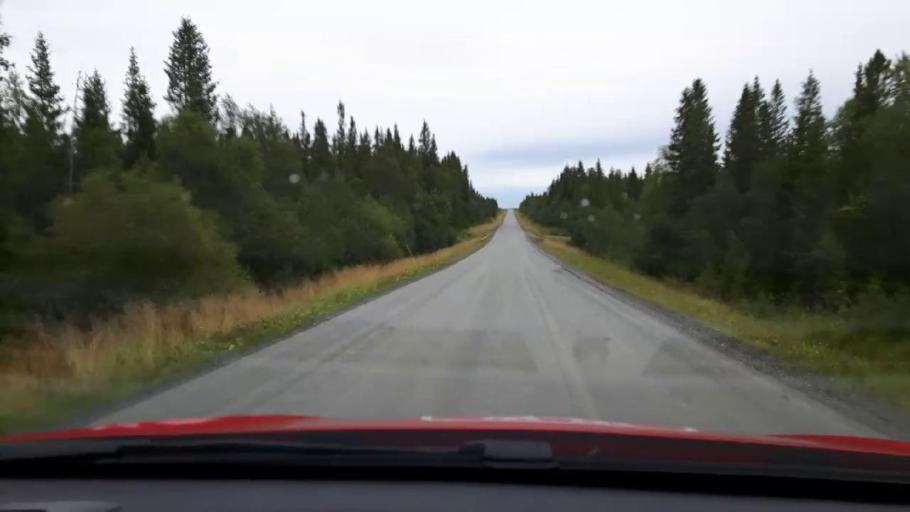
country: SE
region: Jaemtland
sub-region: Are Kommun
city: Are
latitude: 63.4499
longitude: 13.2164
